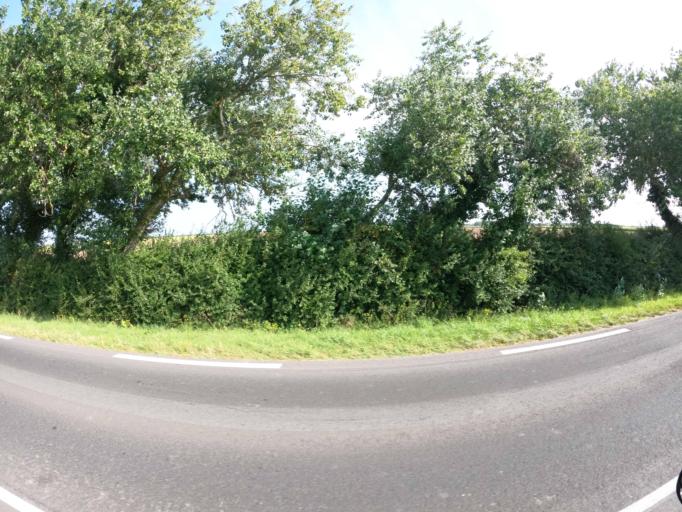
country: FR
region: Pays de la Loire
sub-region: Departement de la Vendee
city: Triaize
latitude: 46.3372
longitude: -1.2726
